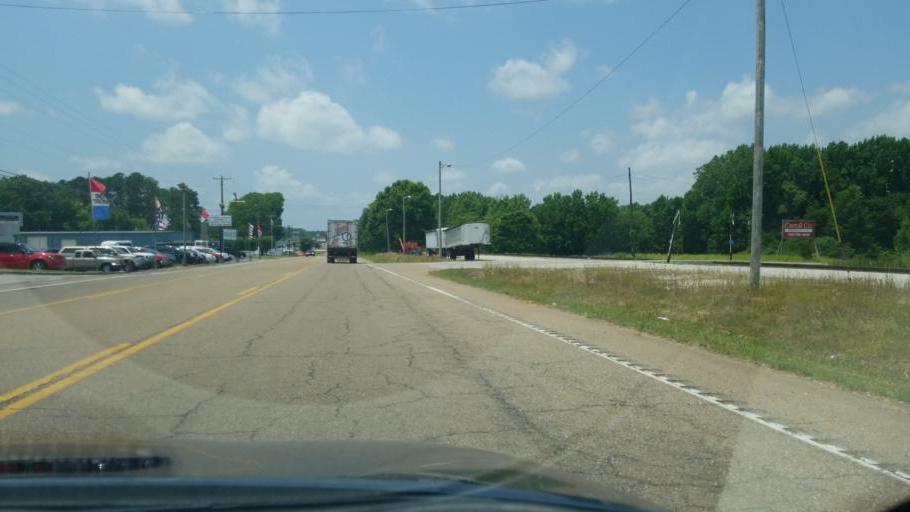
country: US
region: Tennessee
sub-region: Carroll County
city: Huntingdon
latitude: 36.0098
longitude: -88.3990
